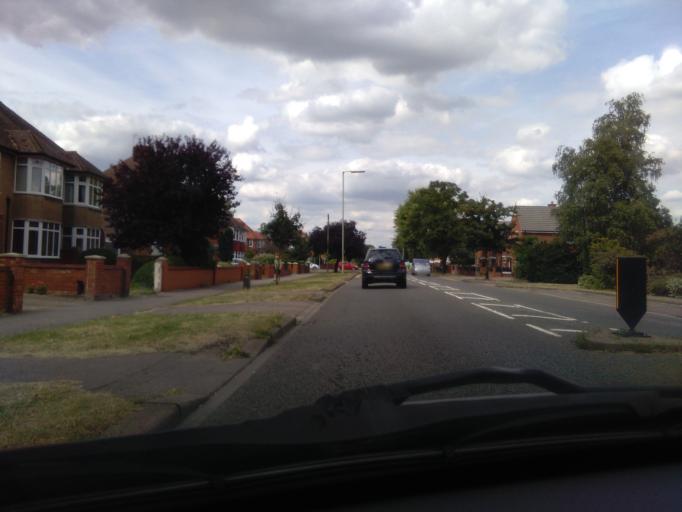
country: GB
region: England
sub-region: Bedford
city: Bedford
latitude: 52.1373
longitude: -0.4446
